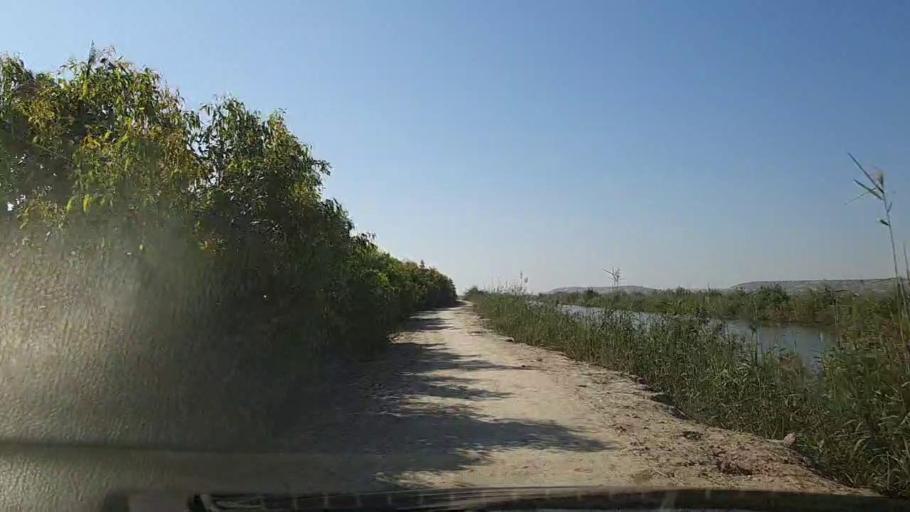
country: PK
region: Sindh
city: Thatta
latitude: 24.6924
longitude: 67.8946
